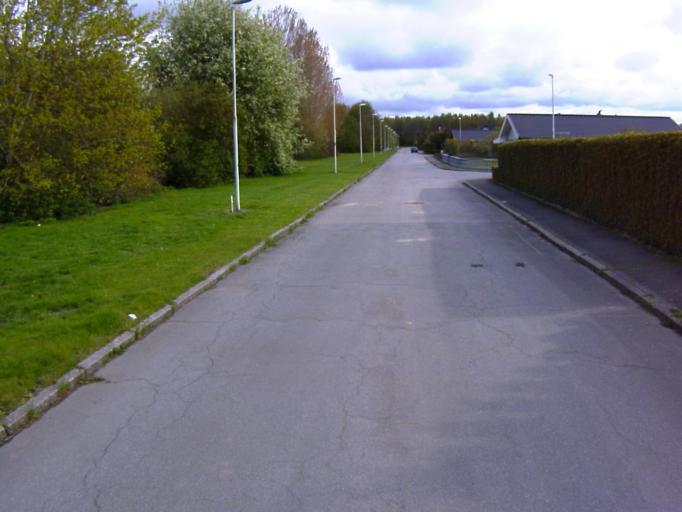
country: SE
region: Skane
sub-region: Kristianstads Kommun
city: Kristianstad
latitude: 56.0486
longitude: 14.1893
